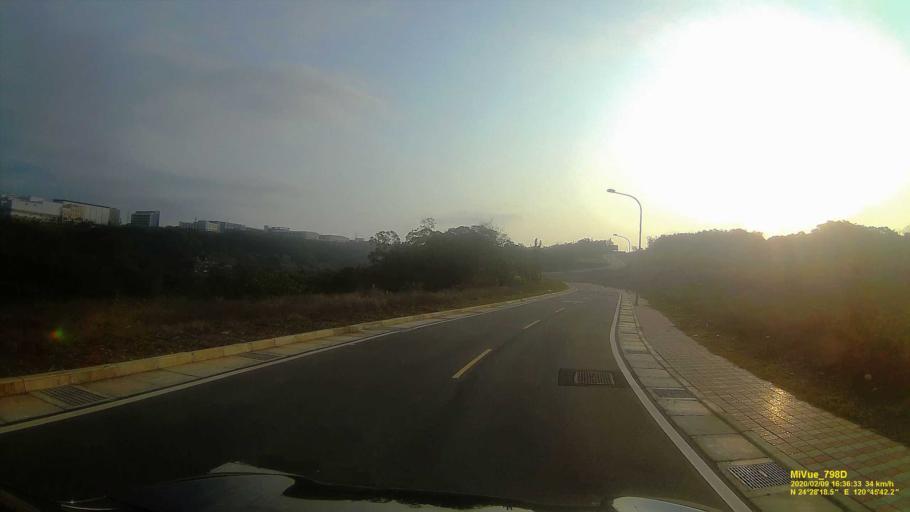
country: TW
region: Taiwan
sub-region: Miaoli
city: Miaoli
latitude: 24.4717
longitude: 120.7616
